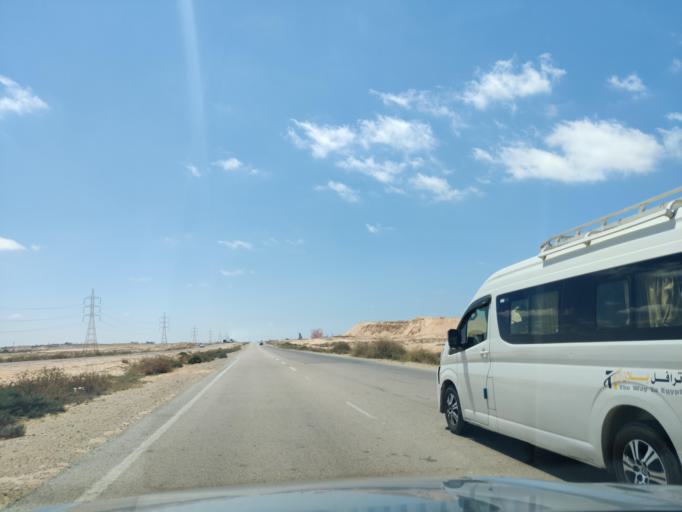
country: EG
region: Muhafazat Matruh
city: Al `Alamayn
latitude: 31.0645
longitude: 28.1923
